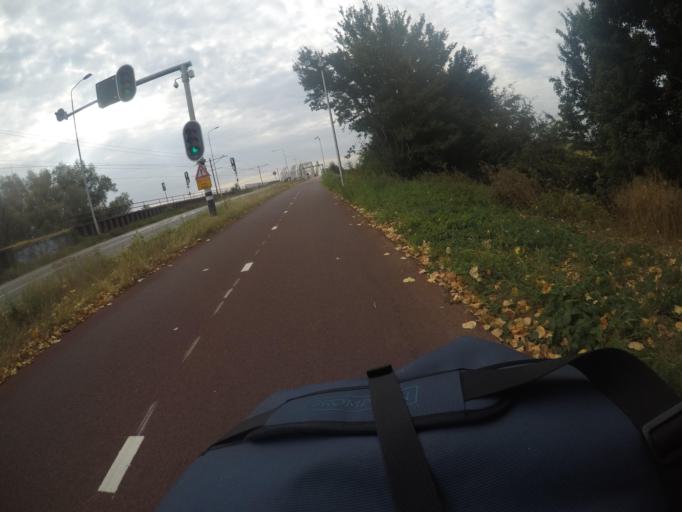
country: NL
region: Gelderland
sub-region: Gemeente Westervoort
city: Westervoort
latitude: 51.9714
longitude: 5.9565
